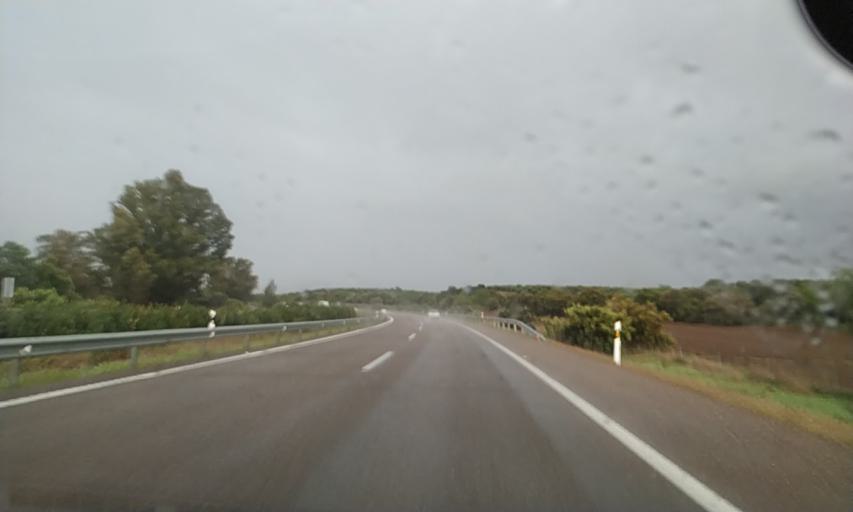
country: ES
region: Extremadura
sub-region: Provincia de Badajoz
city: Torremayor
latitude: 38.8602
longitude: -6.5387
